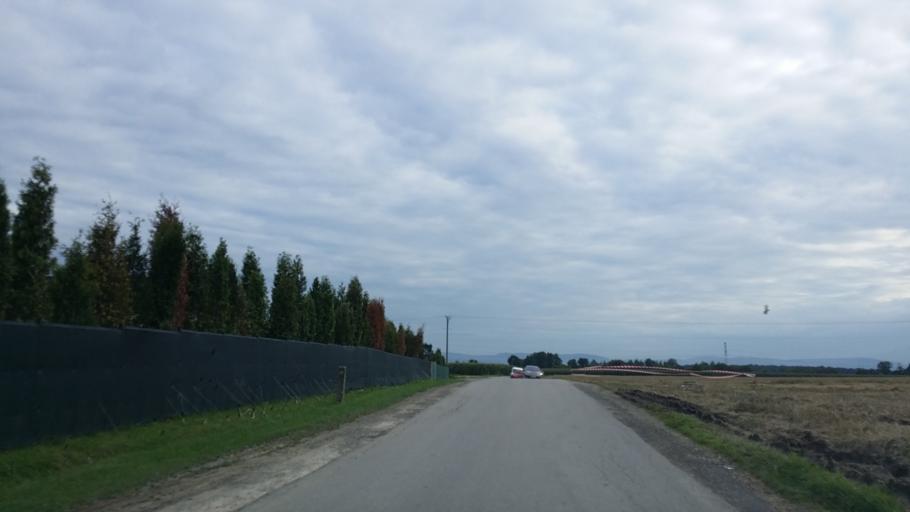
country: PL
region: Lesser Poland Voivodeship
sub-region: Powiat oswiecimski
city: Przeciszow
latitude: 50.0006
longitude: 19.4043
